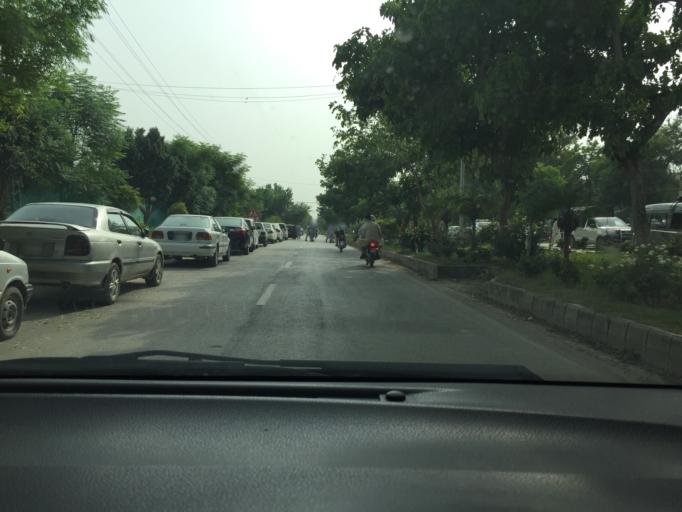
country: PK
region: Islamabad
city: Islamabad
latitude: 33.6772
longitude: 73.0313
